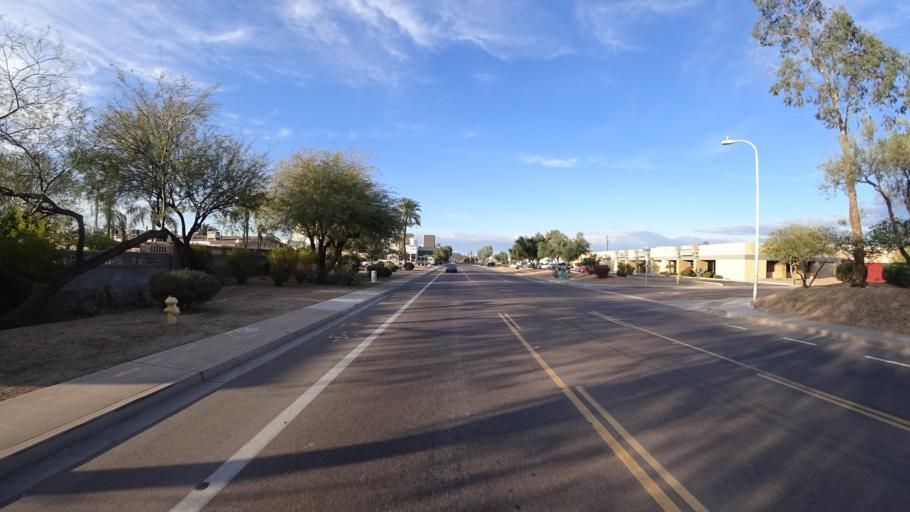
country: US
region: Arizona
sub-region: Maricopa County
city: Tempe Junction
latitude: 33.4027
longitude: -111.9522
